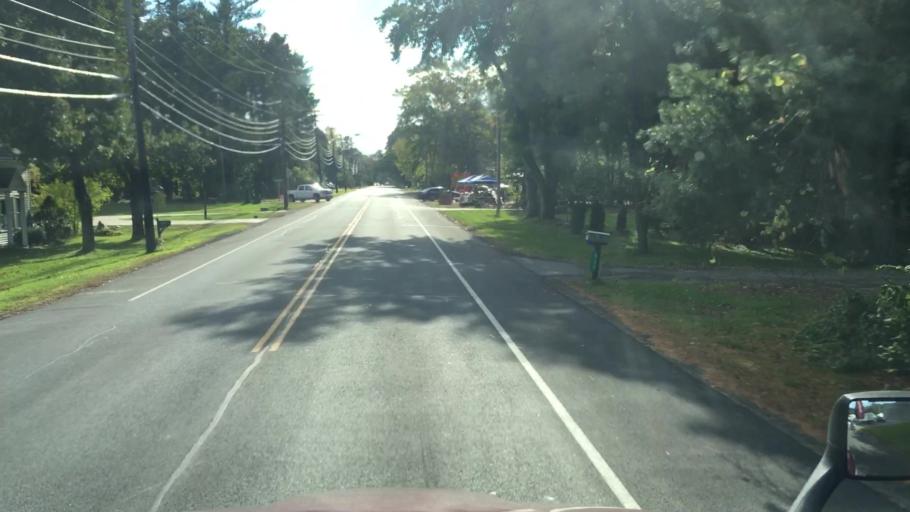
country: US
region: New York
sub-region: Schenectady County
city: East Glenville
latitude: 42.8930
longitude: -73.9202
